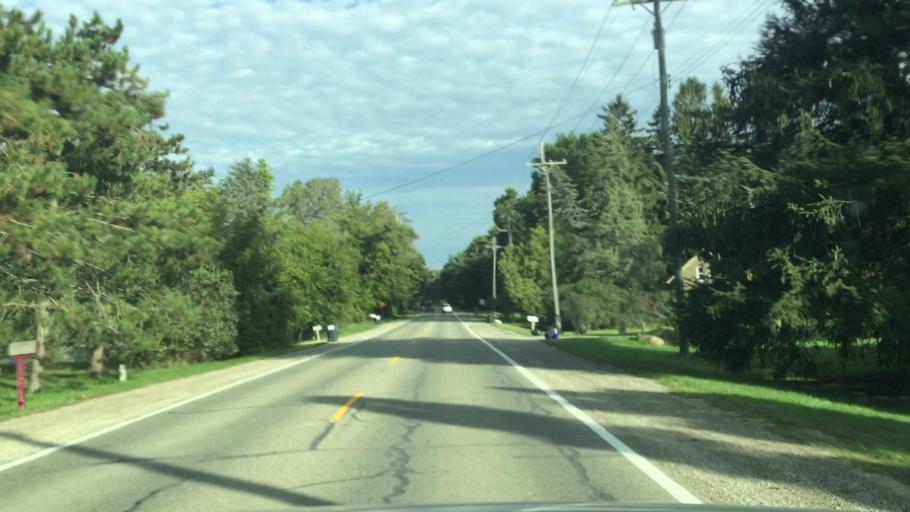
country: US
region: Michigan
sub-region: Livingston County
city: Brighton
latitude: 42.5226
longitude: -83.8575
